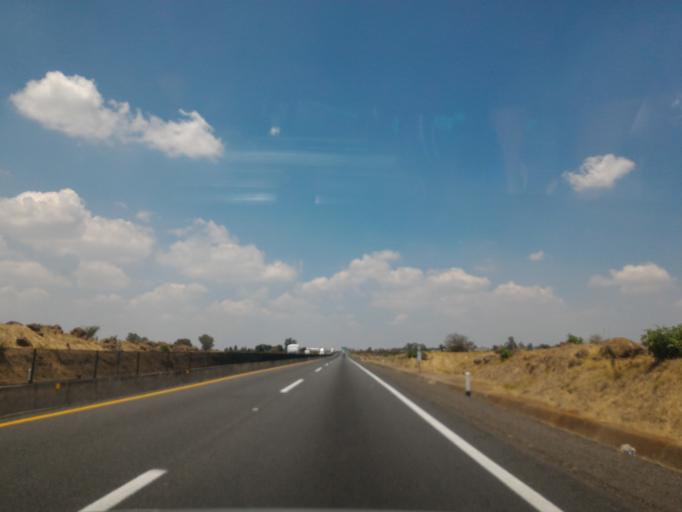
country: MX
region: Jalisco
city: Tepatitlan de Morelos
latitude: 20.8808
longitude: -102.7326
